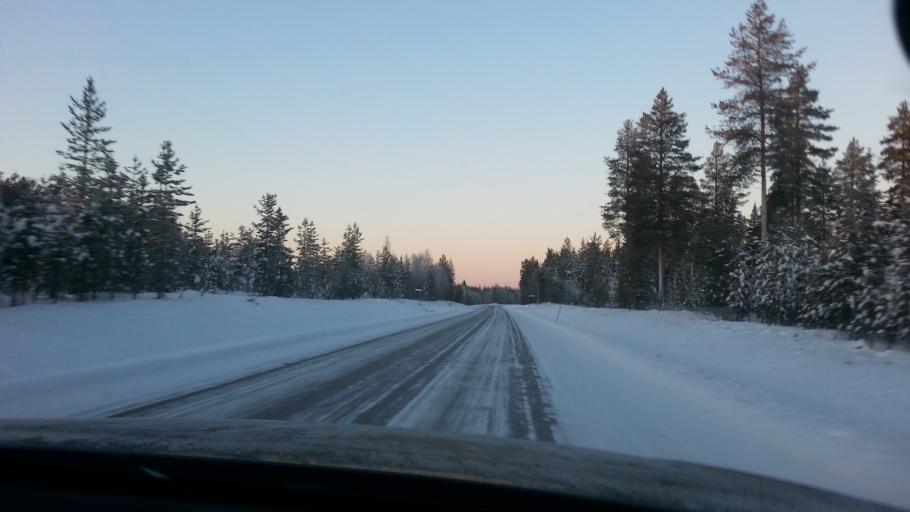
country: FI
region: Lapland
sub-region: Rovaniemi
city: Rovaniemi
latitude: 66.7772
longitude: 25.4539
